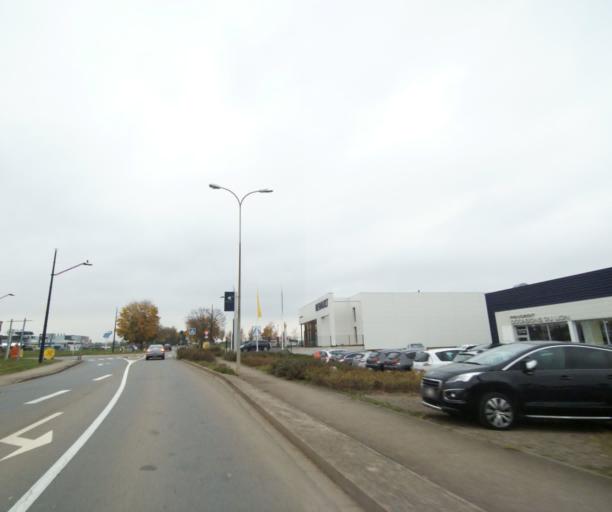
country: FR
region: Lorraine
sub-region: Departement de Meurthe-et-Moselle
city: Briey
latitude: 49.2533
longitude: 5.9464
